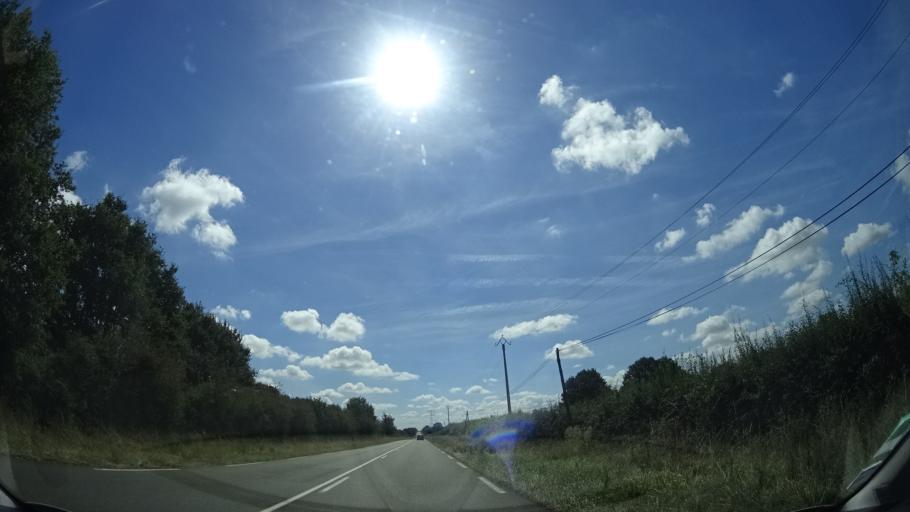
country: FR
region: Pays de la Loire
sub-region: Departement de la Sarthe
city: Auvers-le-Hamon
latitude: 47.9066
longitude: -0.4500
